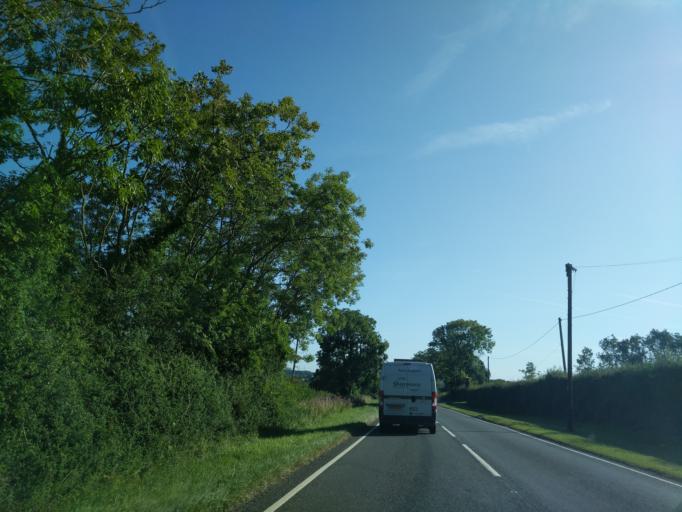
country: GB
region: England
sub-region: District of Rutland
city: Clipsham
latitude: 52.8070
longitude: -0.5446
